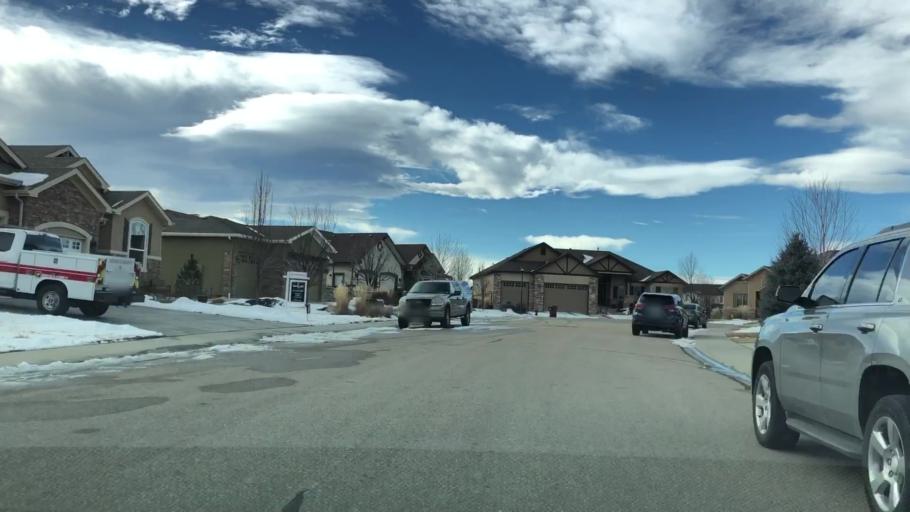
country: US
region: Colorado
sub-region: Weld County
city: Windsor
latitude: 40.4522
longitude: -104.9544
